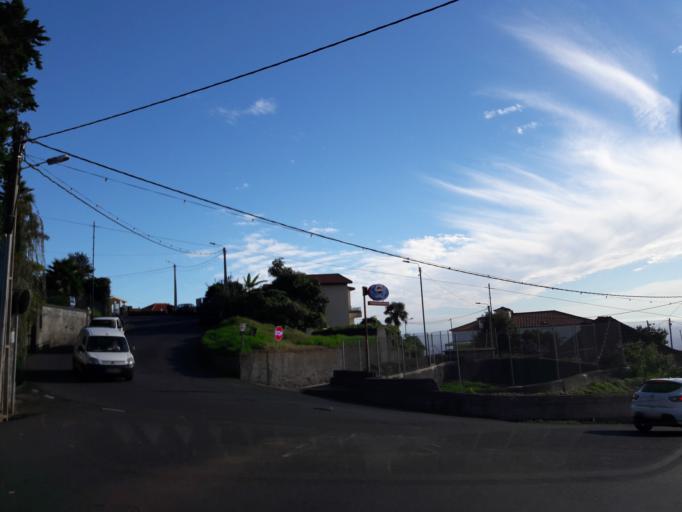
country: PT
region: Madeira
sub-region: Funchal
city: Nossa Senhora do Monte
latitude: 32.6737
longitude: -16.9110
